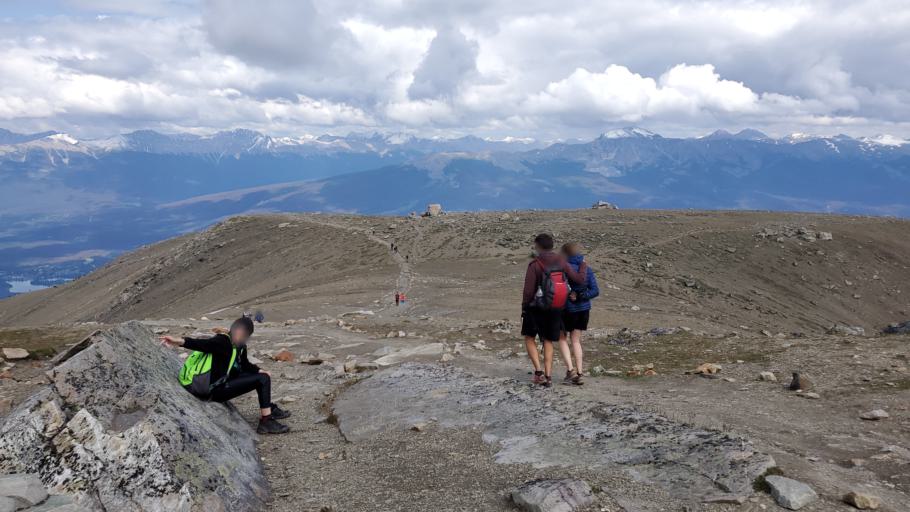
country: CA
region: Alberta
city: Jasper Park Lodge
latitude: 52.8272
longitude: -118.1311
